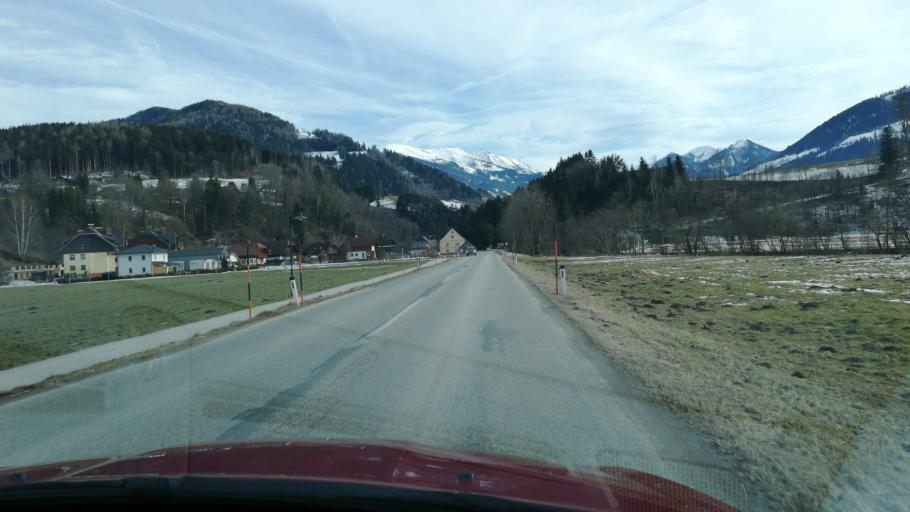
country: AT
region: Styria
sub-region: Politischer Bezirk Liezen
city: Irdning
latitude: 47.5000
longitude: 14.0984
